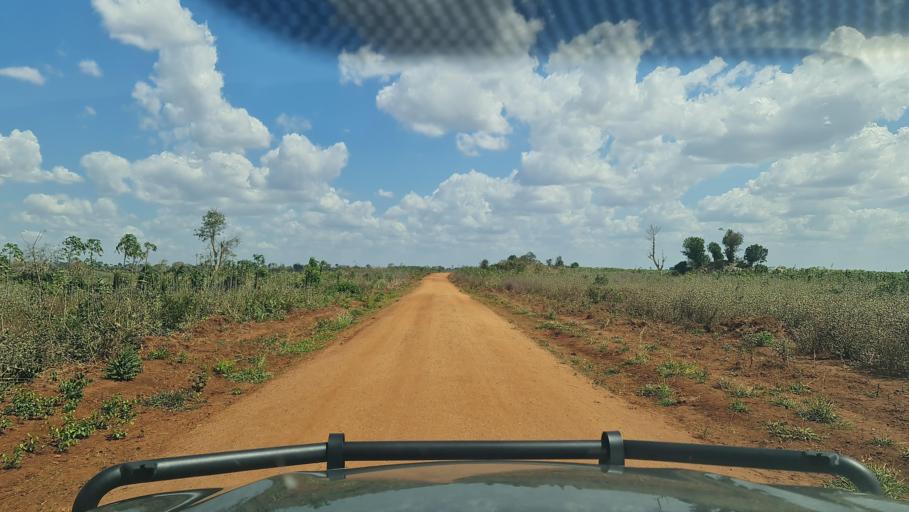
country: MZ
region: Nampula
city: Ilha de Mocambique
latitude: -14.8787
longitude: 40.0226
